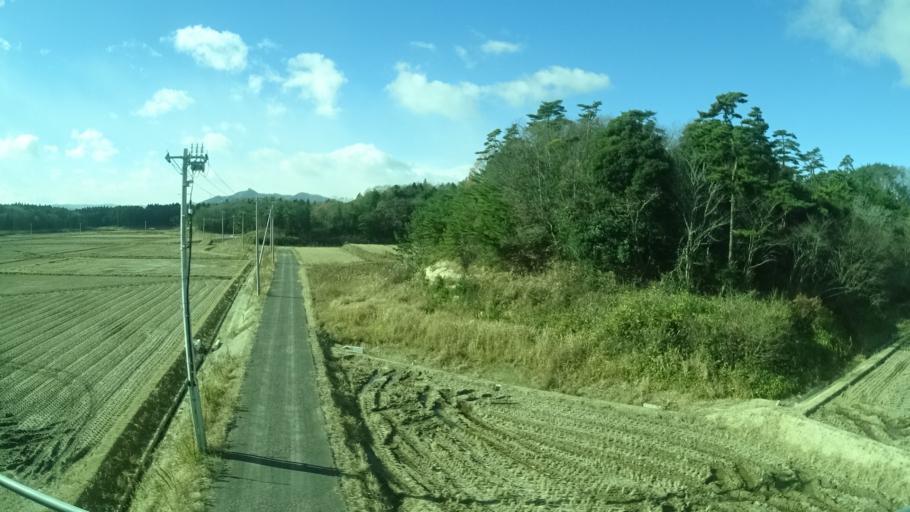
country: JP
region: Miyagi
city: Watari
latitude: 37.9023
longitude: 140.9161
